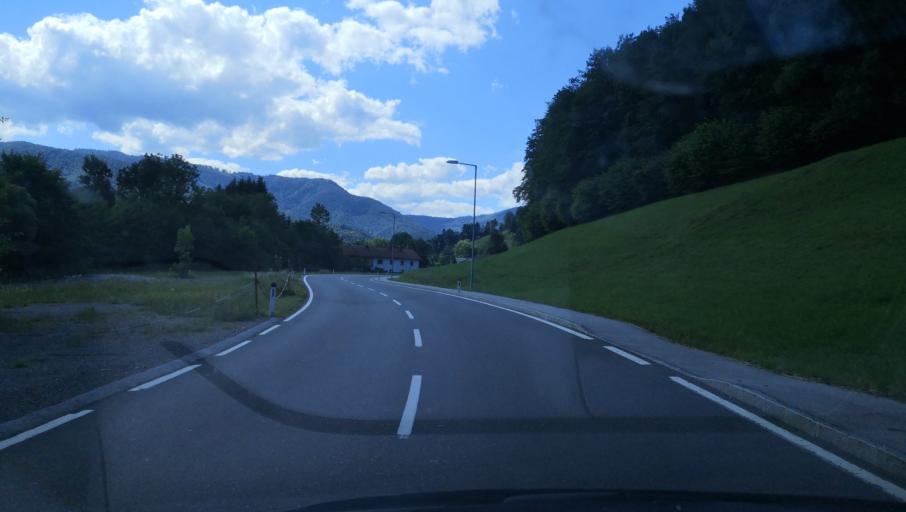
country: AT
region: Lower Austria
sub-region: Politischer Bezirk Scheibbs
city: Gresten
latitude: 47.9653
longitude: 15.0233
